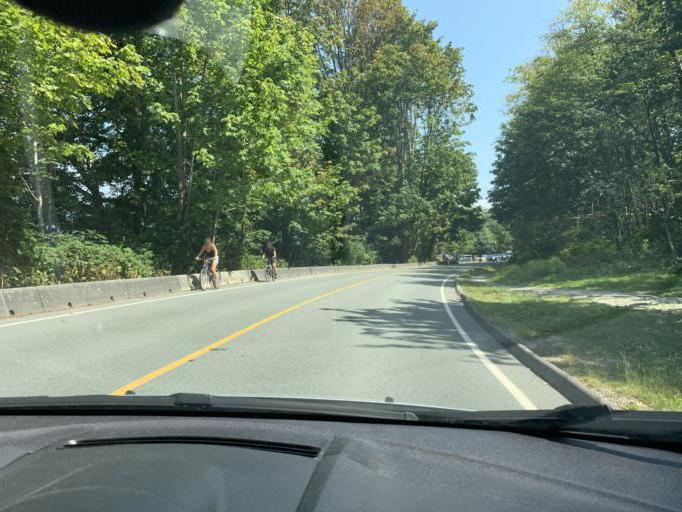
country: CA
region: British Columbia
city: West End
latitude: 49.2792
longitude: -123.2435
